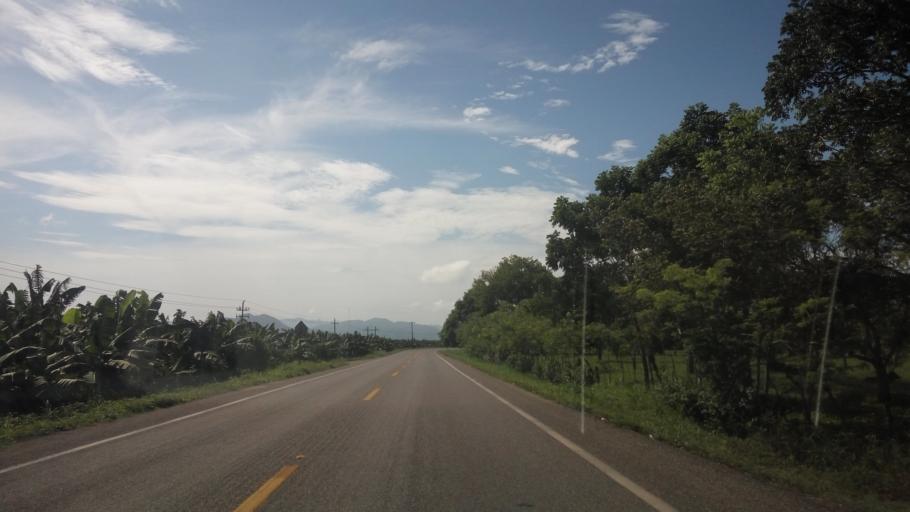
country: MX
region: Tabasco
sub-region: Teapa
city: Eureka y Belen
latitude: 17.6263
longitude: -92.9630
